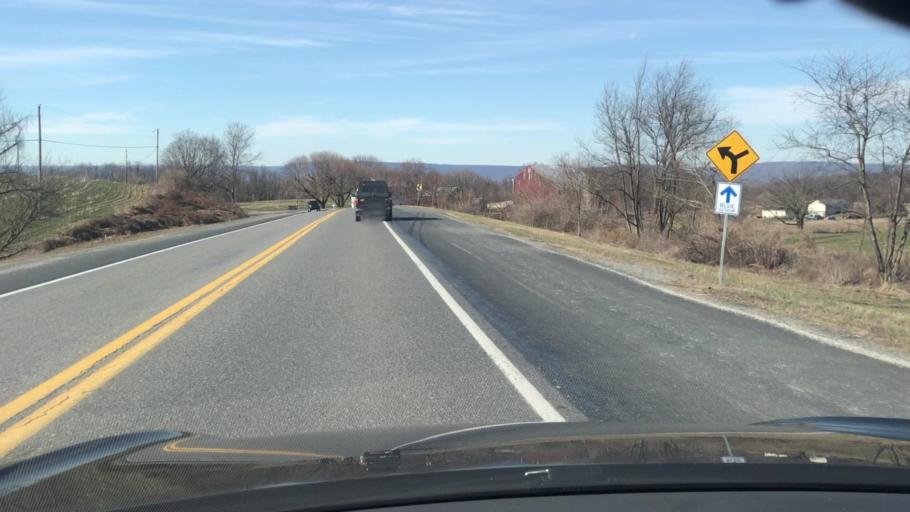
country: US
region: Pennsylvania
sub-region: Cumberland County
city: Newville
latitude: 40.1248
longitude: -77.3452
